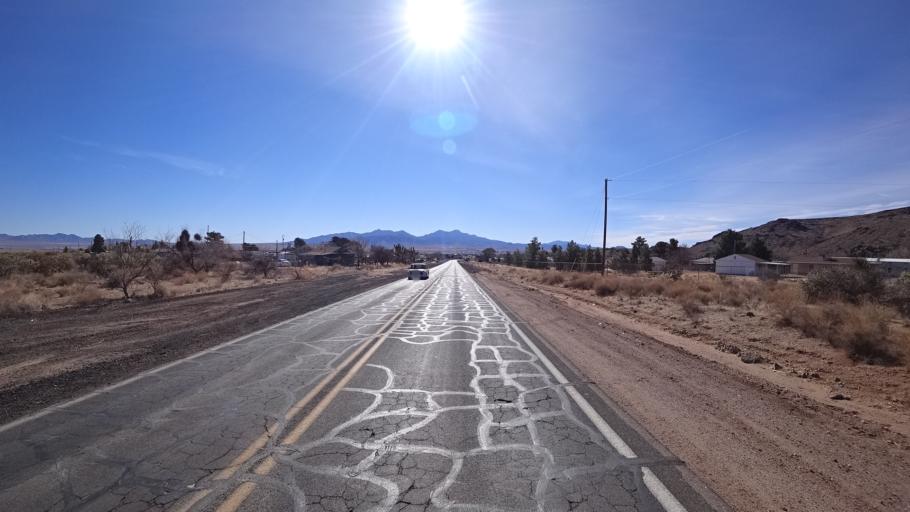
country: US
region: Arizona
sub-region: Mohave County
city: New Kingman-Butler
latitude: 35.2736
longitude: -114.0466
